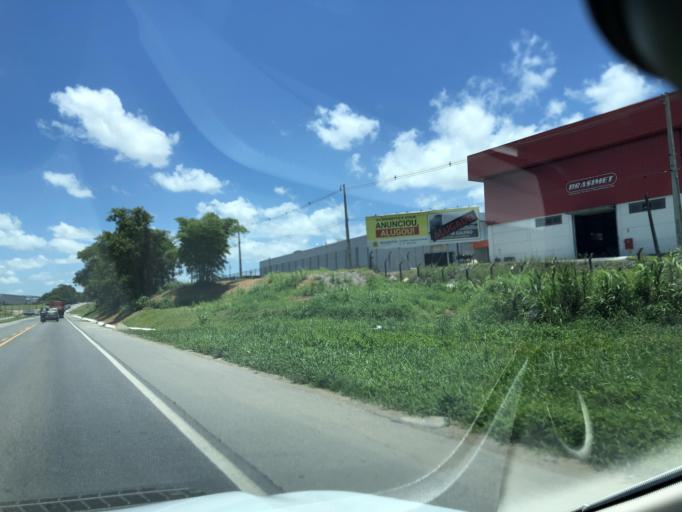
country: BR
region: Santa Catarina
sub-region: Joinville
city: Joinville
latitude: -26.4231
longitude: -48.7833
